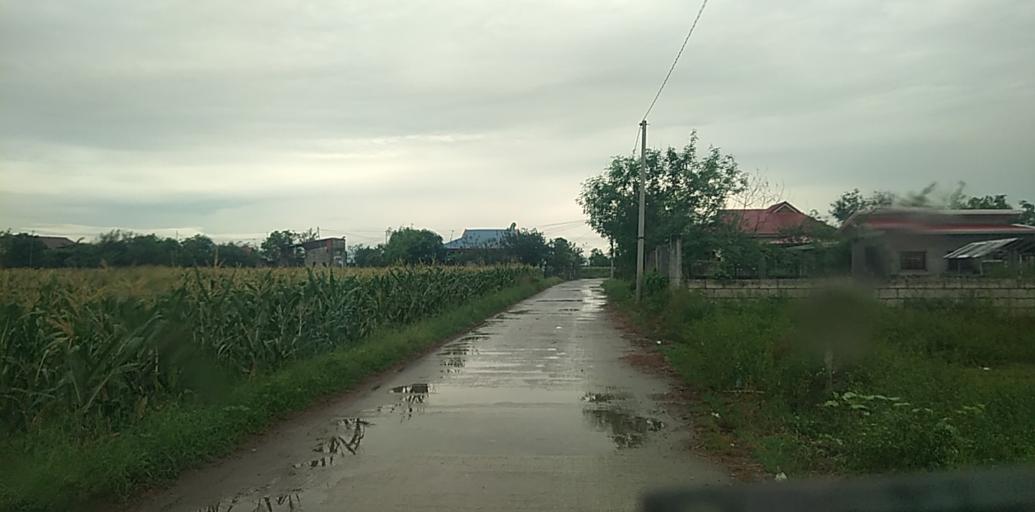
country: PH
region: Central Luzon
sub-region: Province of Pampanga
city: Anao
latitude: 15.1431
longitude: 120.7274
